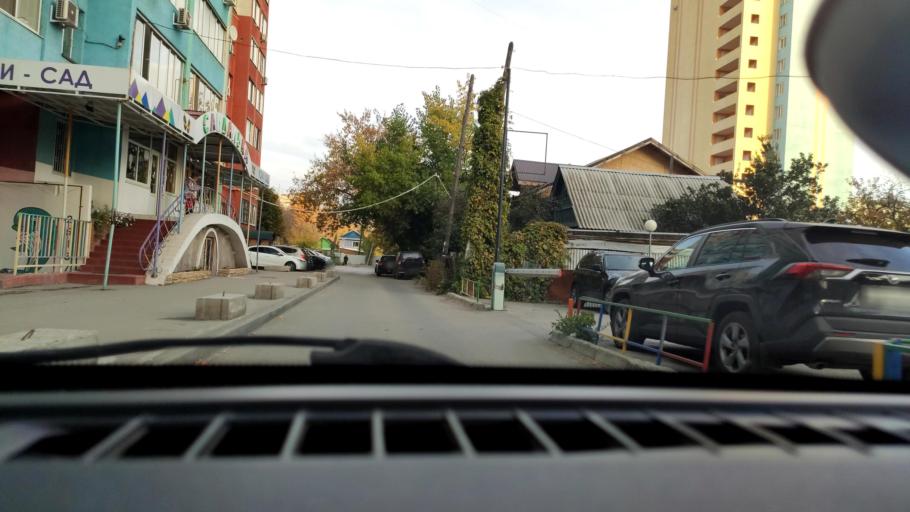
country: RU
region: Samara
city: Samara
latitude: 53.1989
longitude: 50.1800
